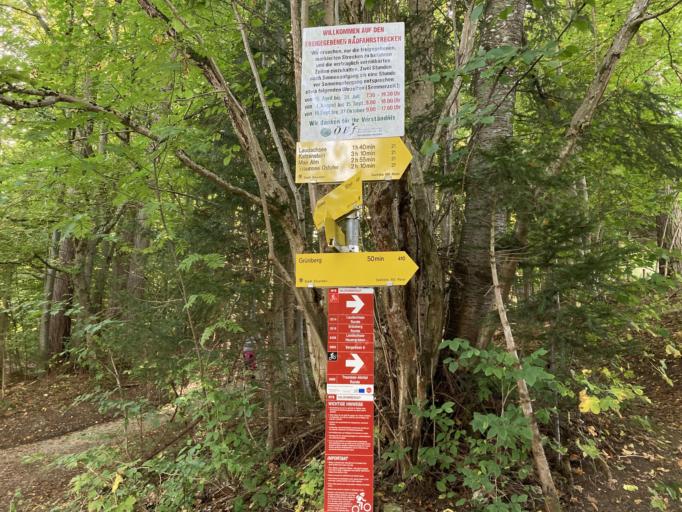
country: AT
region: Upper Austria
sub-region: Politischer Bezirk Gmunden
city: Gmunden
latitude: 47.9108
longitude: 13.8236
